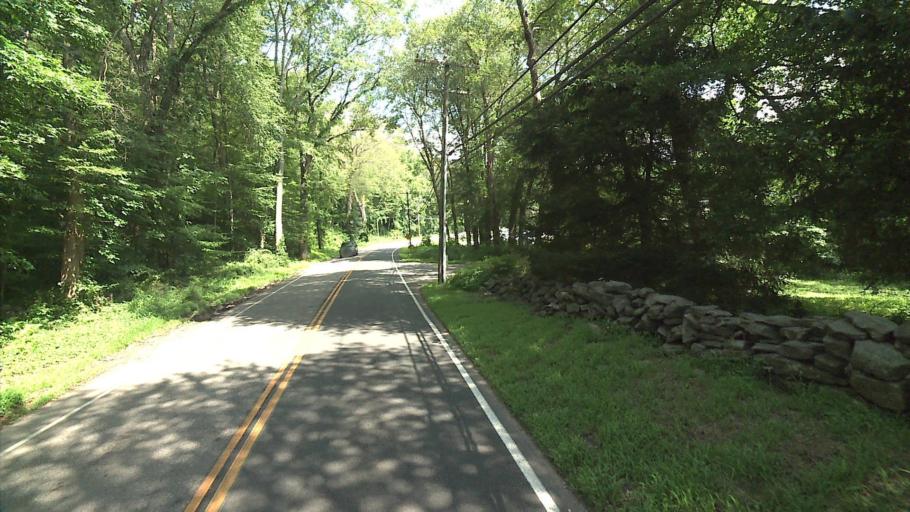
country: US
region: Connecticut
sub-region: Middlesex County
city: Essex Village
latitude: 41.3433
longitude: -72.4147
